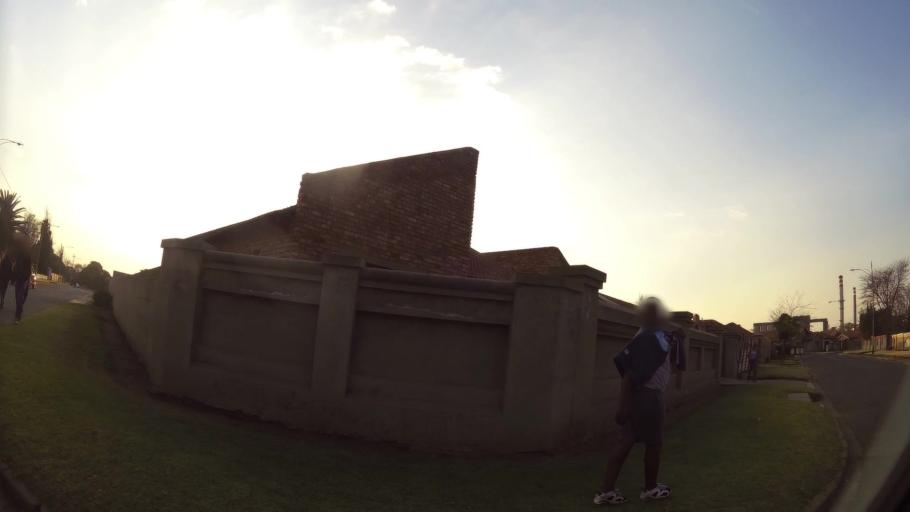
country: ZA
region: Gauteng
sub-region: Ekurhuleni Metropolitan Municipality
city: Springs
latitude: -26.2665
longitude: 28.4098
